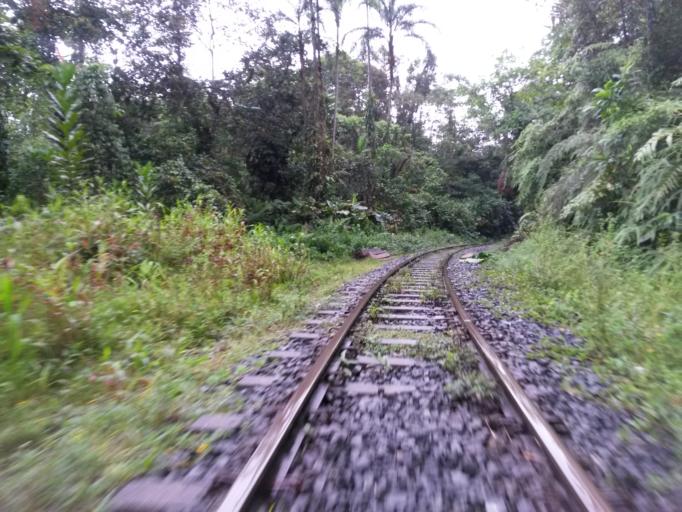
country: CO
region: Valle del Cauca
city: Buenaventura
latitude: 3.8501
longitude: -76.9134
